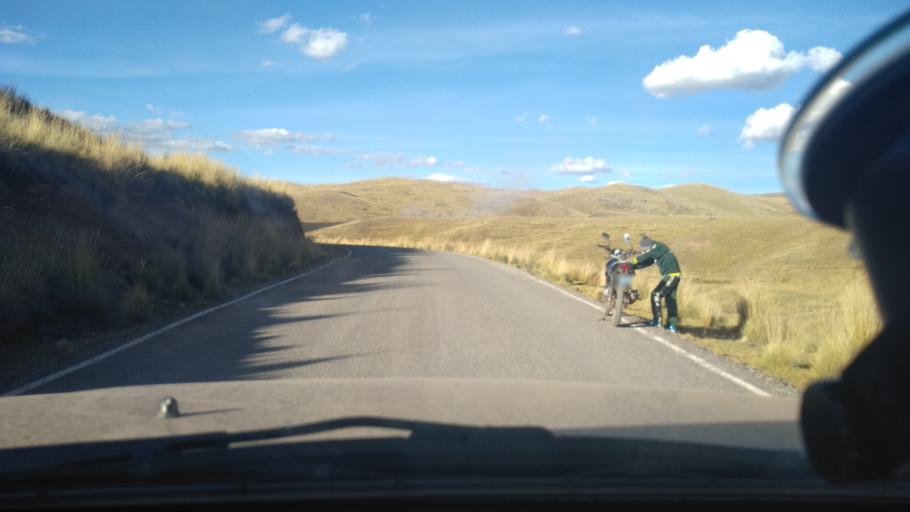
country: PE
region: Cusco
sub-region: Provincia de Canas
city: Ccaquiracunca
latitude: -14.2828
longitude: -71.4503
